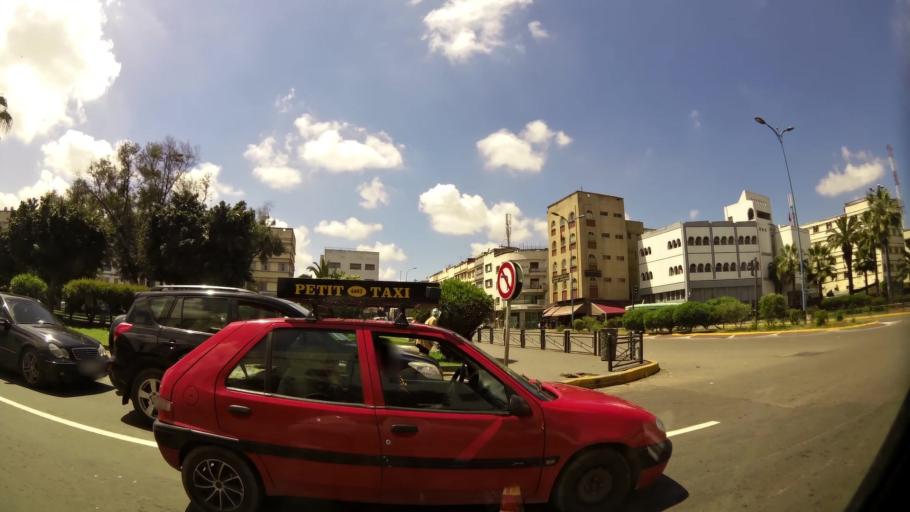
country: MA
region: Grand Casablanca
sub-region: Casablanca
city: Casablanca
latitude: 33.5563
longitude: -7.5721
